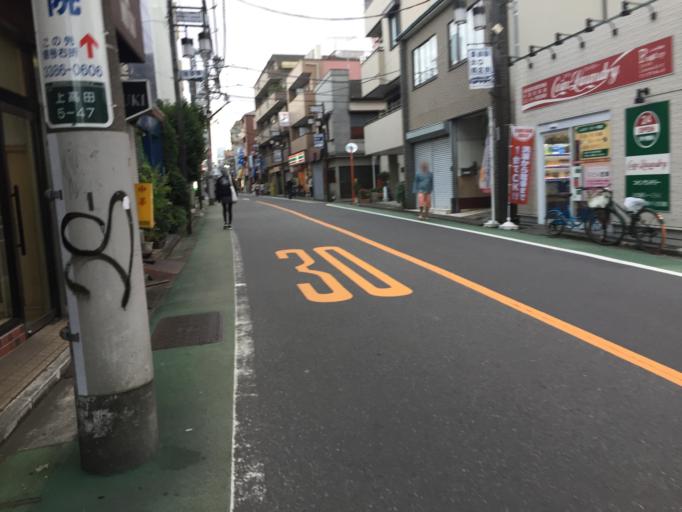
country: JP
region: Tokyo
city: Tokyo
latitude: 35.7185
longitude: 139.6733
